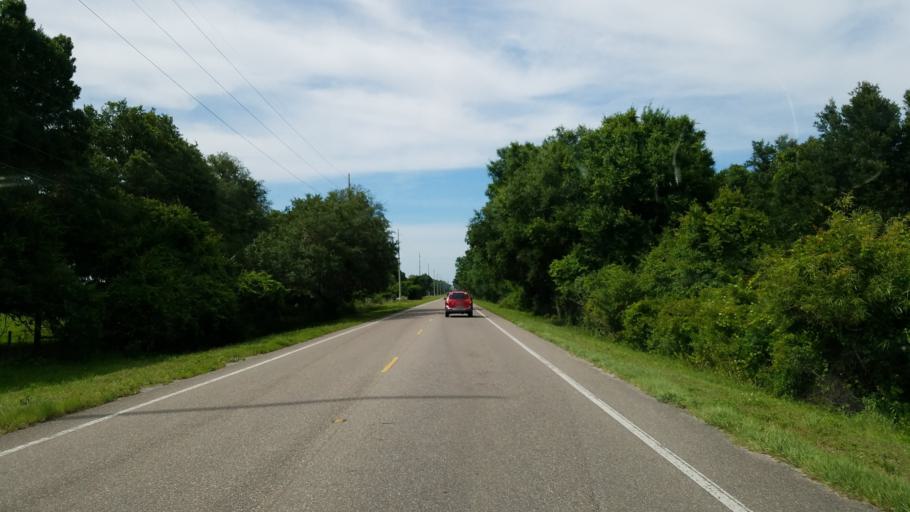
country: US
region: Florida
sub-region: Hillsborough County
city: Balm
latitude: 27.6785
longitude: -82.1462
